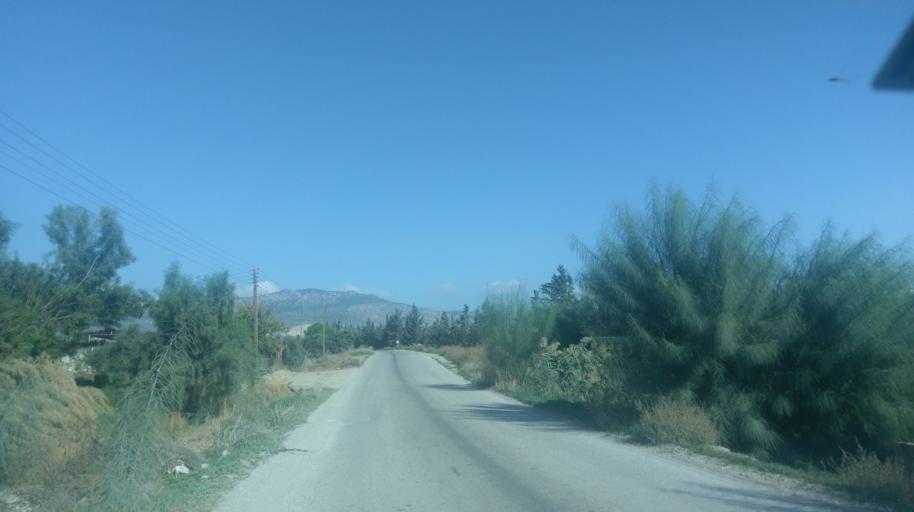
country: CY
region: Lefkosia
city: Nicosia
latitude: 35.2287
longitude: 33.4189
